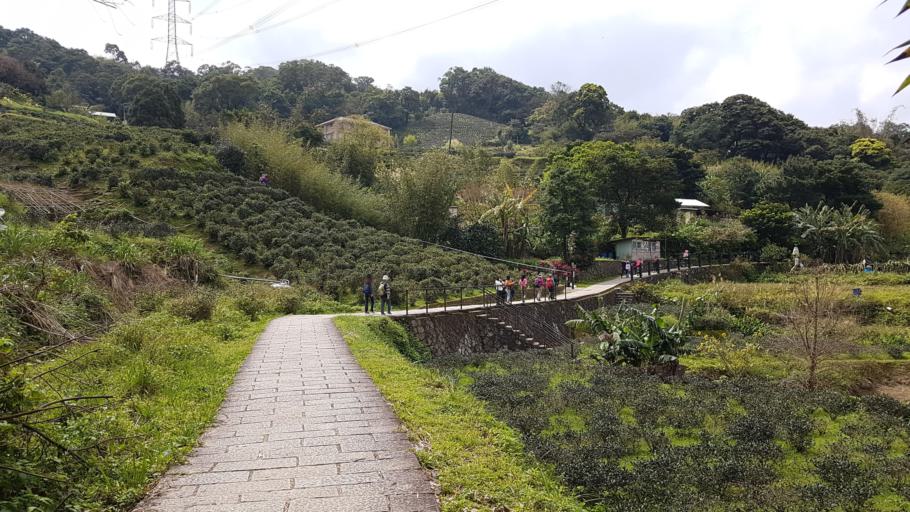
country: TW
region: Taipei
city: Taipei
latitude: 24.9674
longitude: 121.5838
